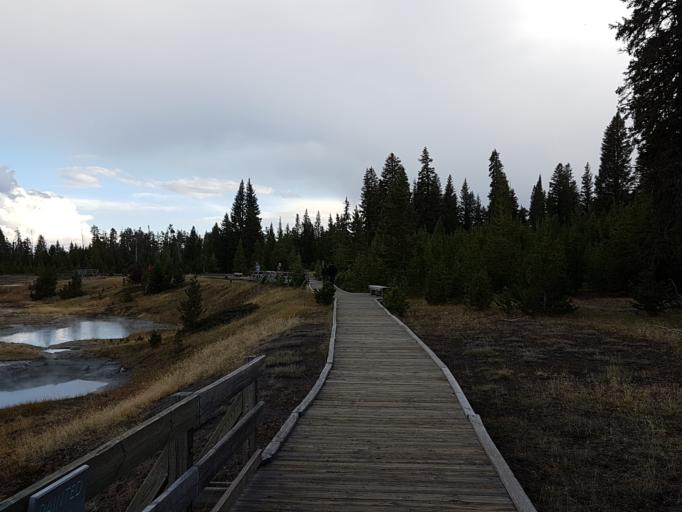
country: US
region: Montana
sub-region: Gallatin County
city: West Yellowstone
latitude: 44.4170
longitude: -110.5732
